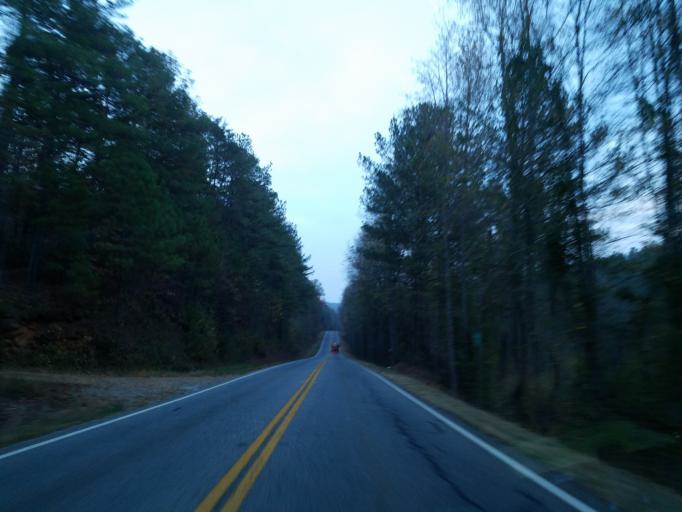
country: US
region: Georgia
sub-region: Pickens County
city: Jasper
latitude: 34.5411
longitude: -84.5809
